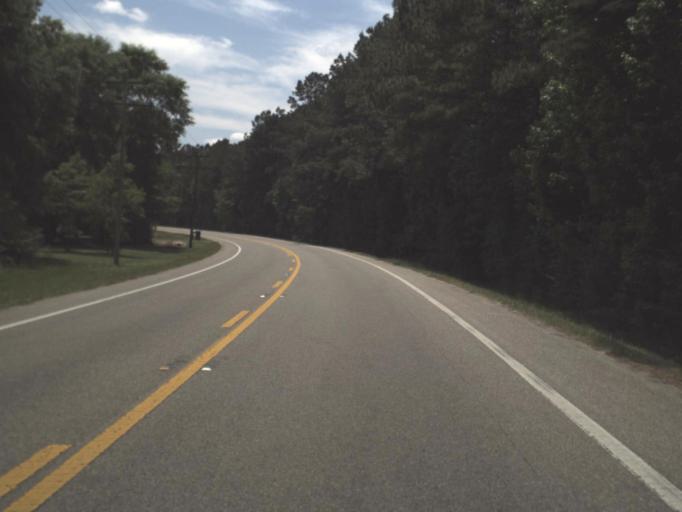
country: US
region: Florida
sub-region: Calhoun County
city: Blountstown
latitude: 30.5327
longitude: -85.1331
